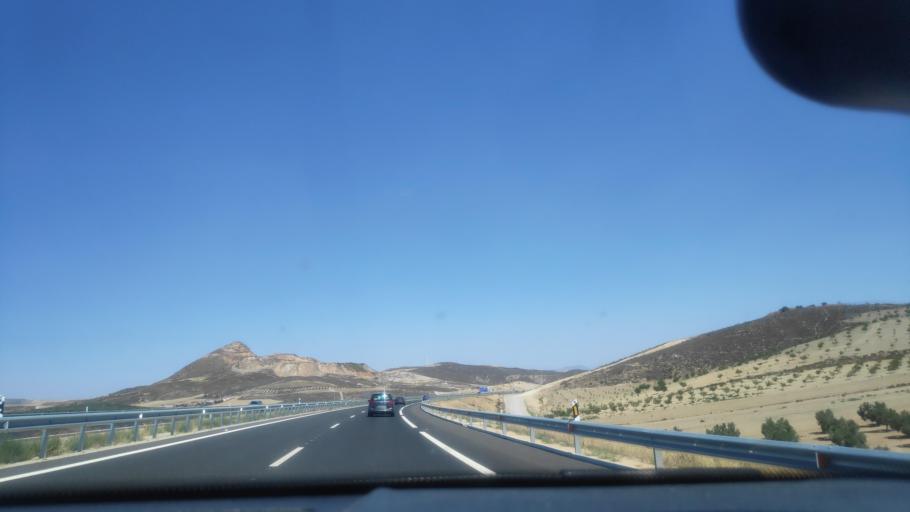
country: ES
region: Andalusia
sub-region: Provincia de Granada
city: Alhendin
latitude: 37.0904
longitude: -3.6707
